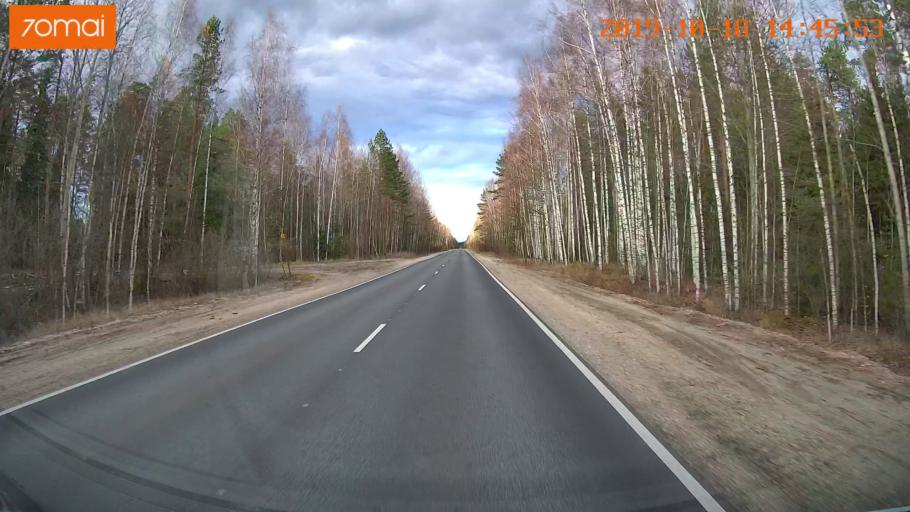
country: RU
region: Vladimir
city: Velikodvorskiy
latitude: 55.3623
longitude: 40.6798
